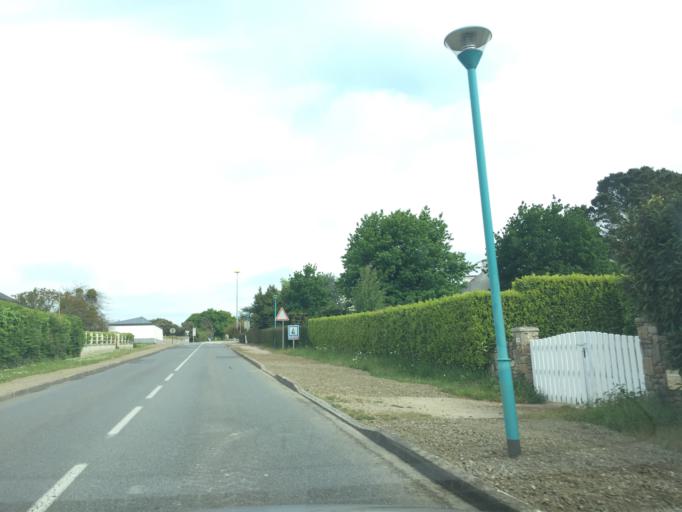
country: FR
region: Brittany
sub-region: Departement des Cotes-d'Armor
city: Saint-Cast-le-Guildo
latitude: 48.6182
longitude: -2.2493
